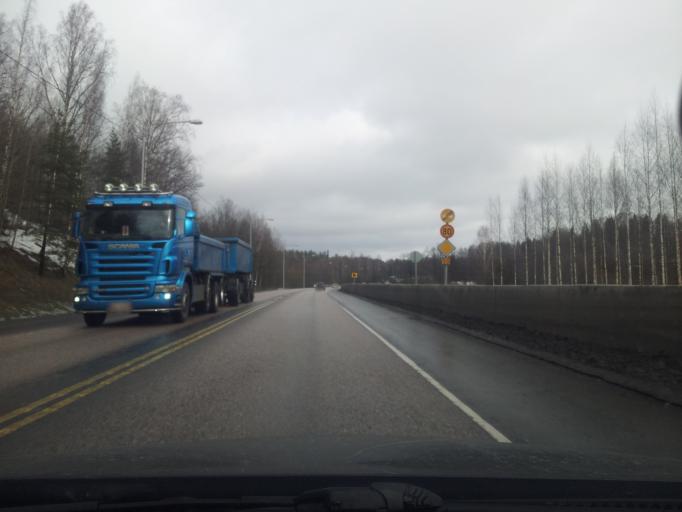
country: FI
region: Uusimaa
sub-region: Helsinki
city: Espoo
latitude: 60.1933
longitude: 24.5817
